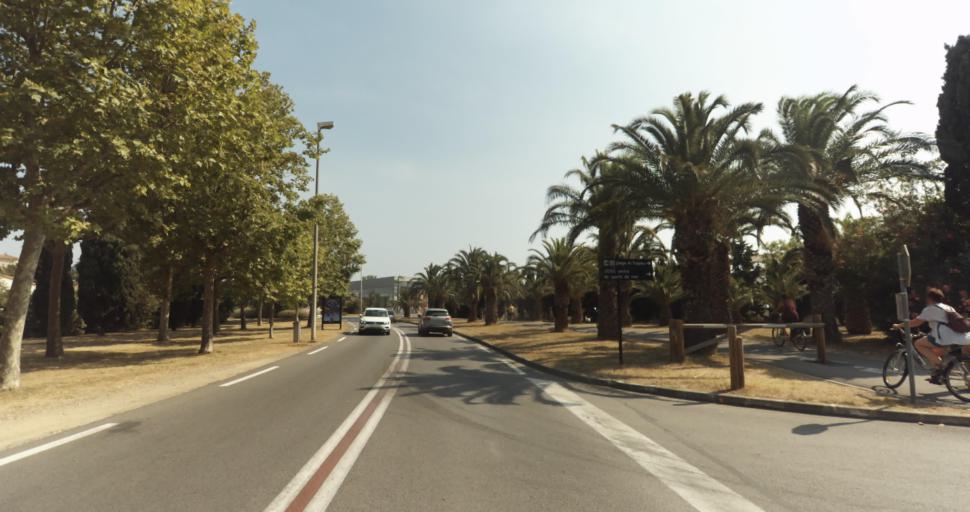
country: FR
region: Languedoc-Roussillon
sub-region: Departement des Pyrenees-Orientales
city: Saint-Cyprien-Plage
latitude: 42.6139
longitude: 3.0335
